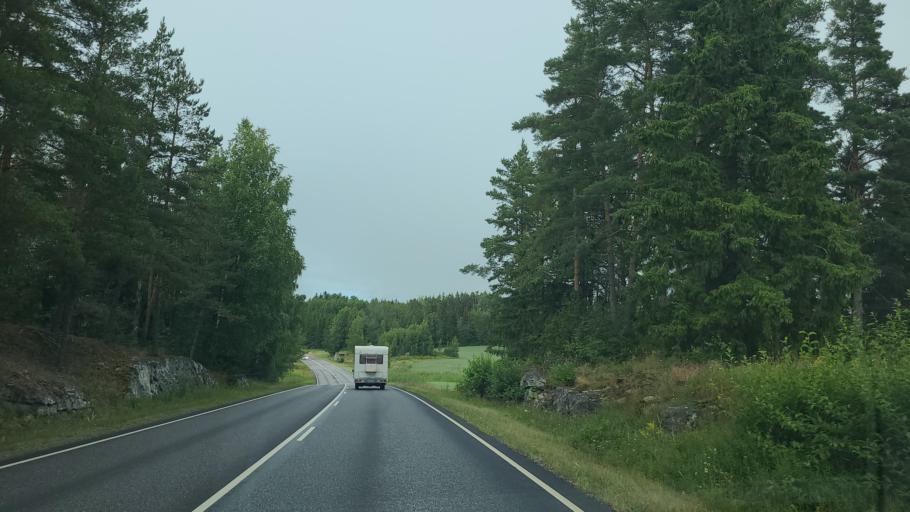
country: FI
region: Varsinais-Suomi
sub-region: Turku
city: Sauvo
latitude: 60.2977
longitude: 22.6788
